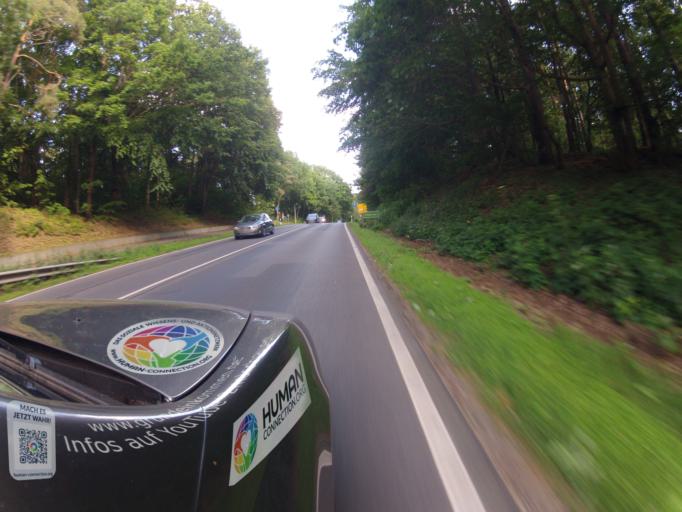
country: DE
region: Mecklenburg-Vorpommern
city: Loddin
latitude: 54.0371
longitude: 14.0180
